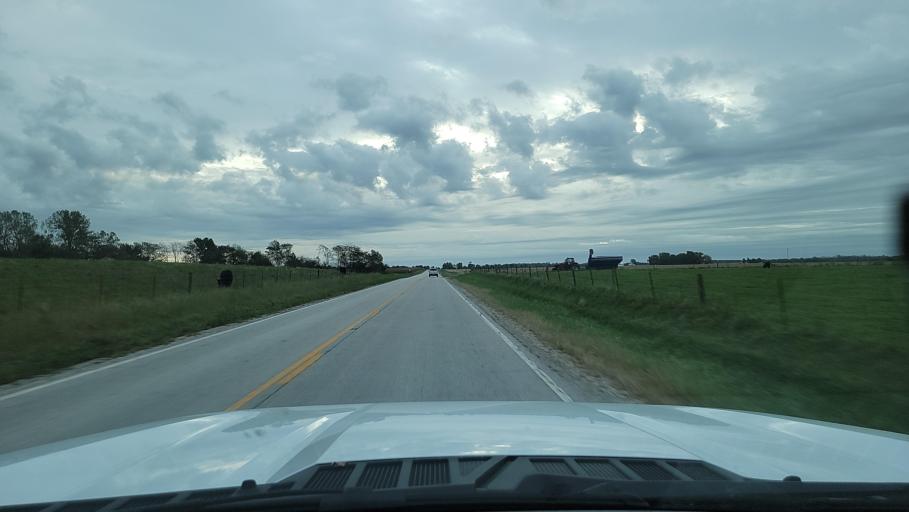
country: US
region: Illinois
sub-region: Schuyler County
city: Rushville
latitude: 40.1537
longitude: -90.5494
